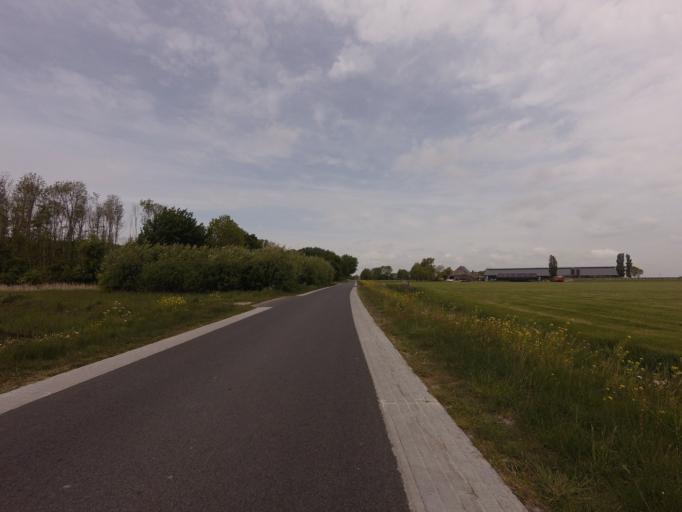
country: NL
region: Friesland
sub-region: Sudwest Fryslan
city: Bolsward
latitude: 53.0943
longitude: 5.4774
